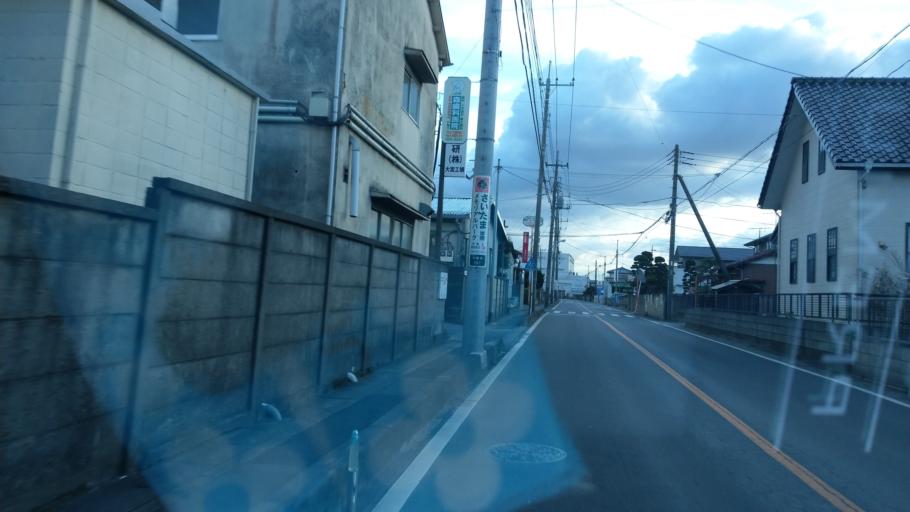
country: JP
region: Saitama
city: Yono
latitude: 35.8971
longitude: 139.5924
